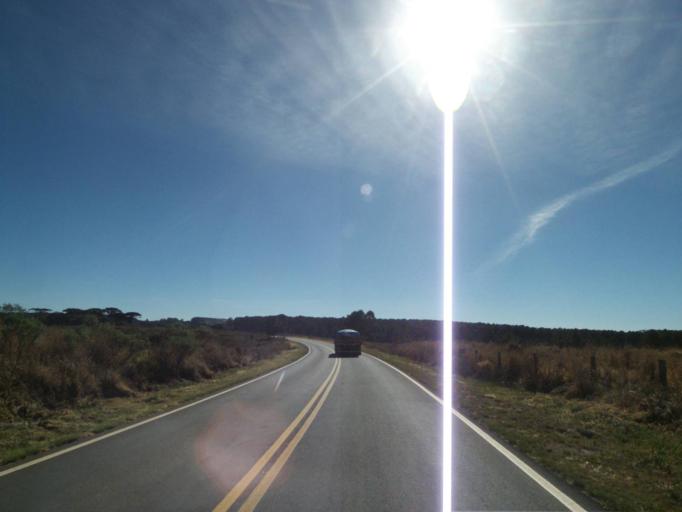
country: BR
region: Parana
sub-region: Castro
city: Castro
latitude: -24.7329
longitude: -50.1814
